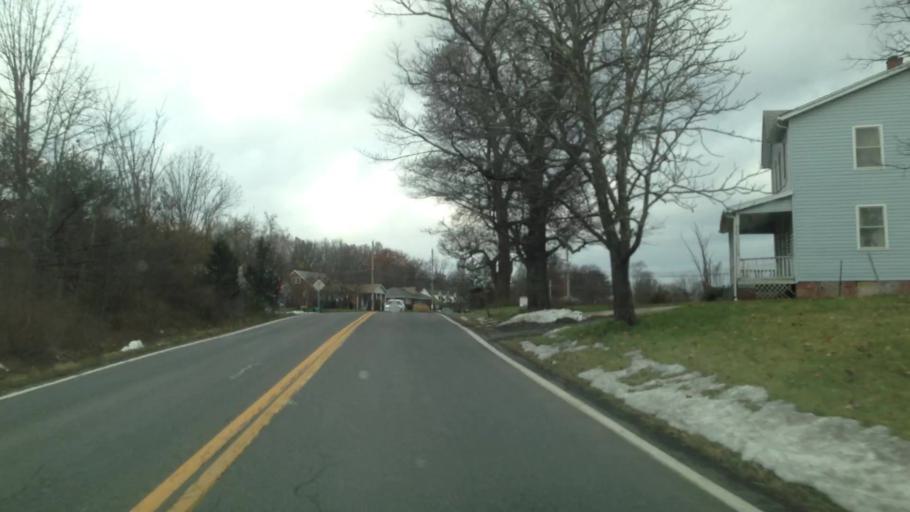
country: US
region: New York
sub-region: Ulster County
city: Glasco
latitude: 42.0306
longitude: -73.9565
